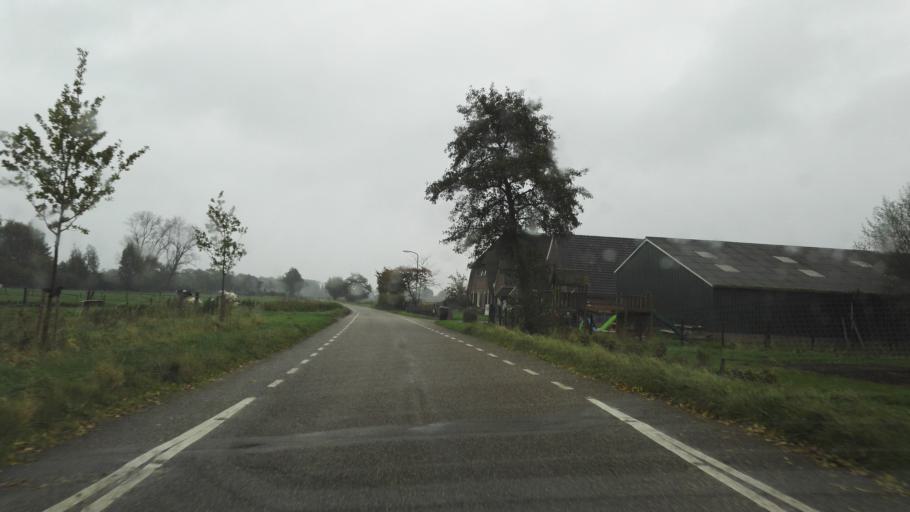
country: NL
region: Gelderland
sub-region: Gemeente Apeldoorn
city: Apeldoorn
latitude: 52.2364
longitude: 6.0207
